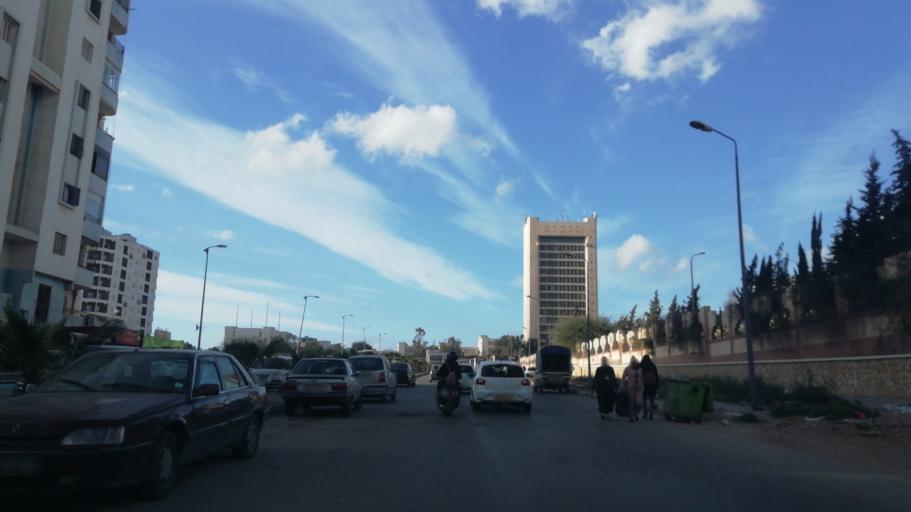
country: DZ
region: Oran
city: Bir el Djir
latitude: 35.7021
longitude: -0.5761
